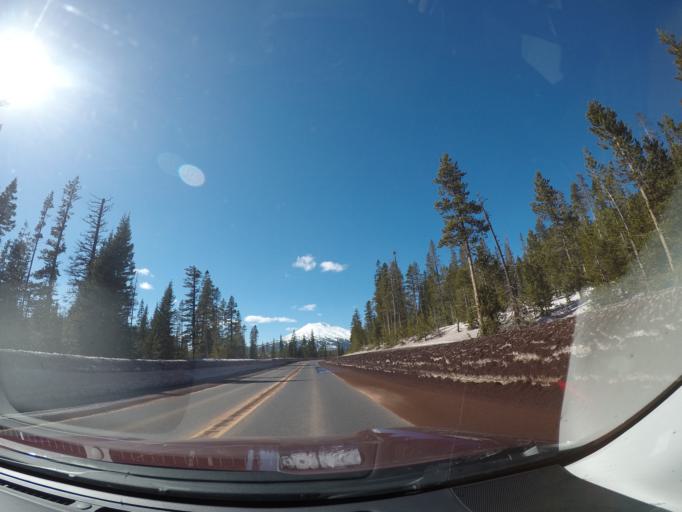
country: US
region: Oregon
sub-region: Deschutes County
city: Sunriver
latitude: 43.9828
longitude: -121.5939
